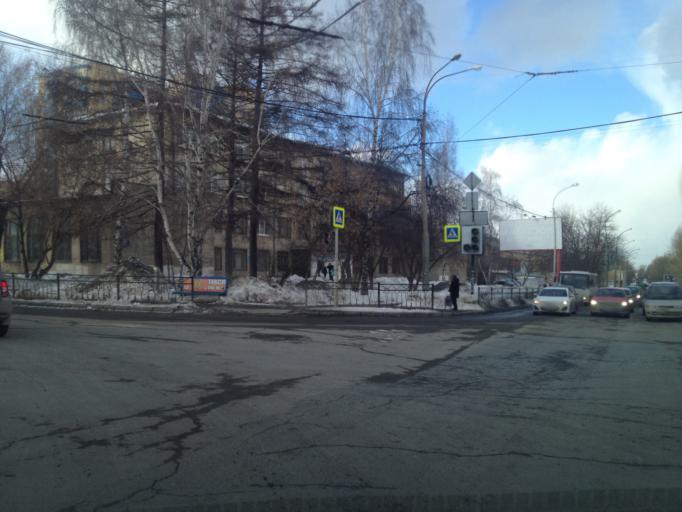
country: RU
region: Sverdlovsk
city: Yekaterinburg
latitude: 56.8608
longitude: 60.6533
